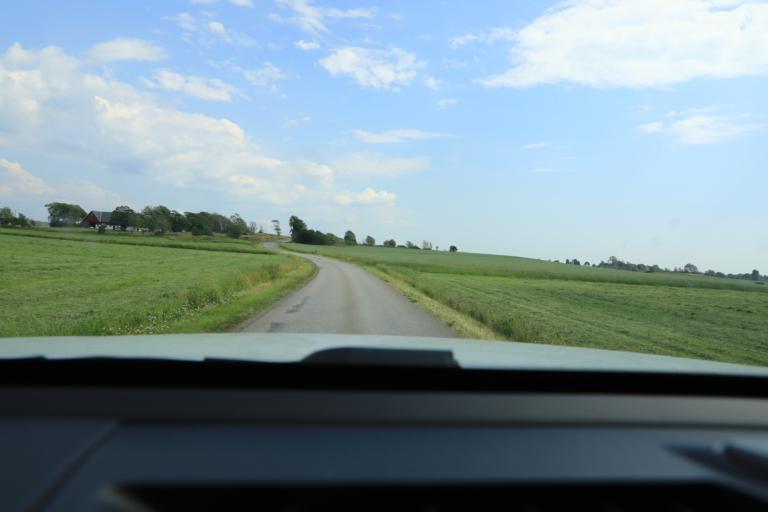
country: SE
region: Halland
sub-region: Varbergs Kommun
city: Varberg
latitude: 57.1389
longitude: 12.3251
